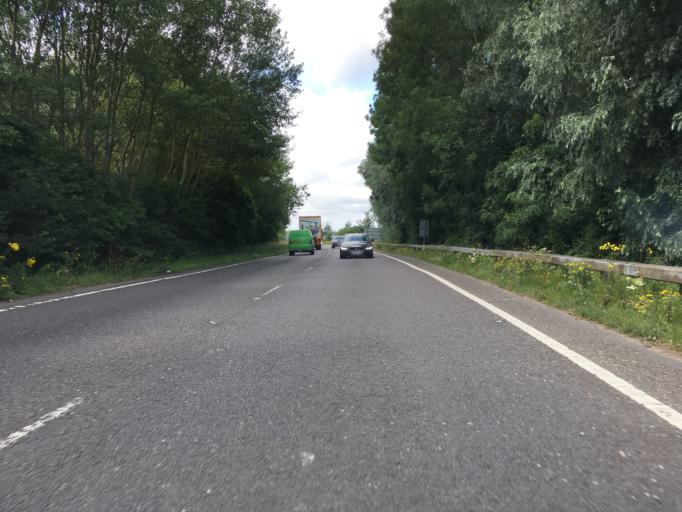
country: GB
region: England
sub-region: East Sussex
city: Pevensey
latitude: 50.8224
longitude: 0.3413
